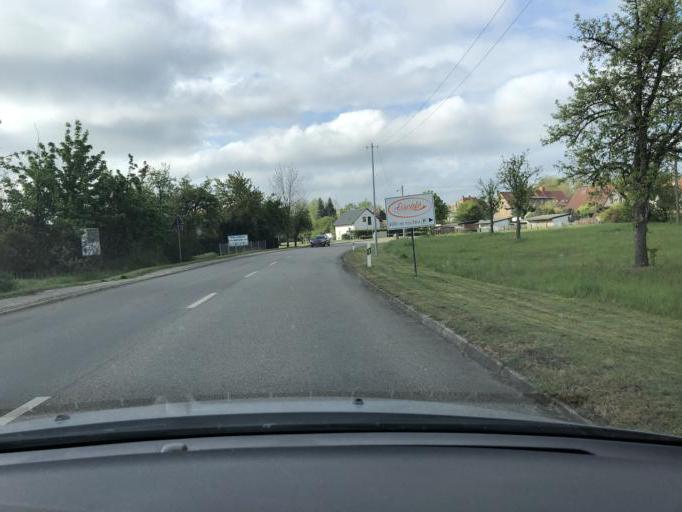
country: DE
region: Saxony
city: Deutzen
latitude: 51.1137
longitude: 12.4299
